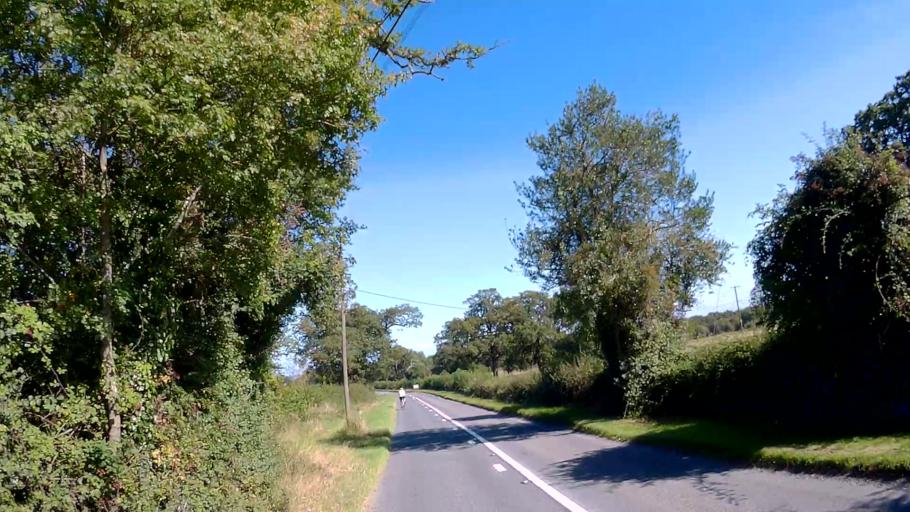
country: GB
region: England
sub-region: West Berkshire
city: Stratfield Mortimer
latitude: 51.3754
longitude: -0.9966
